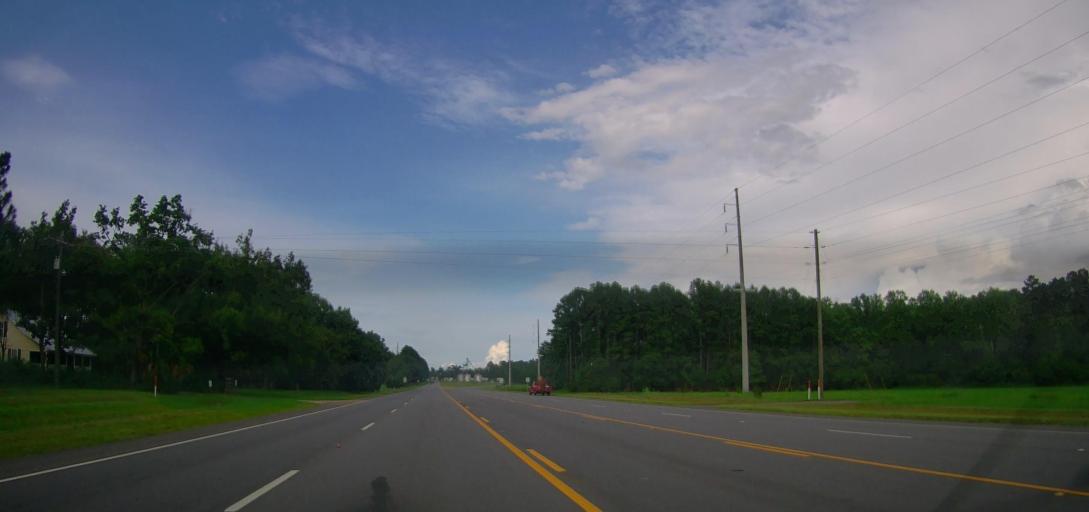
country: US
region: Georgia
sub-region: Wayne County
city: Jesup
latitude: 31.4780
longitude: -82.0283
